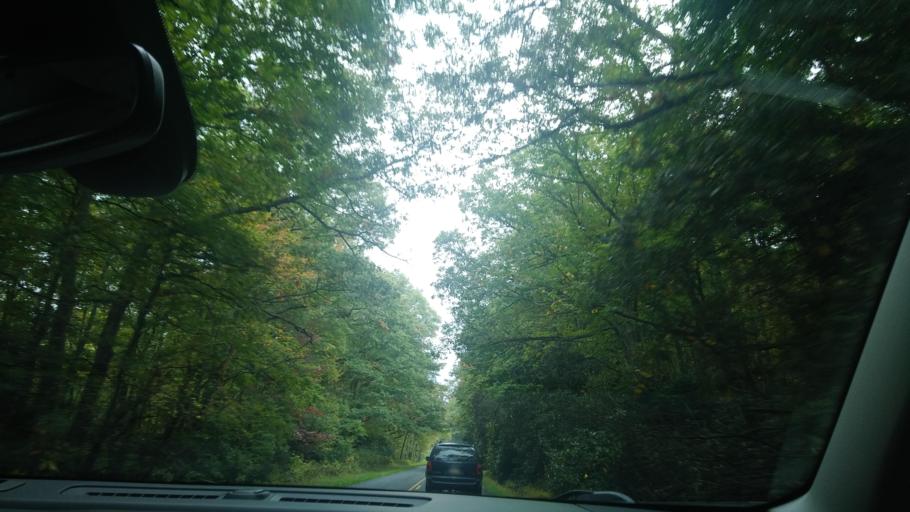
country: US
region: Virginia
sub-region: Carroll County
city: Cana
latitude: 36.6556
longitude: -80.5641
